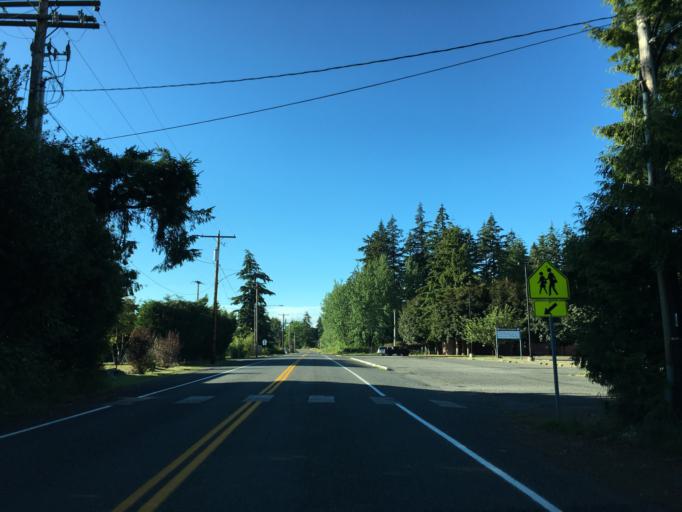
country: US
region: Washington
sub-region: Whatcom County
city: Ferndale
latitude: 48.9185
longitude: -122.6384
